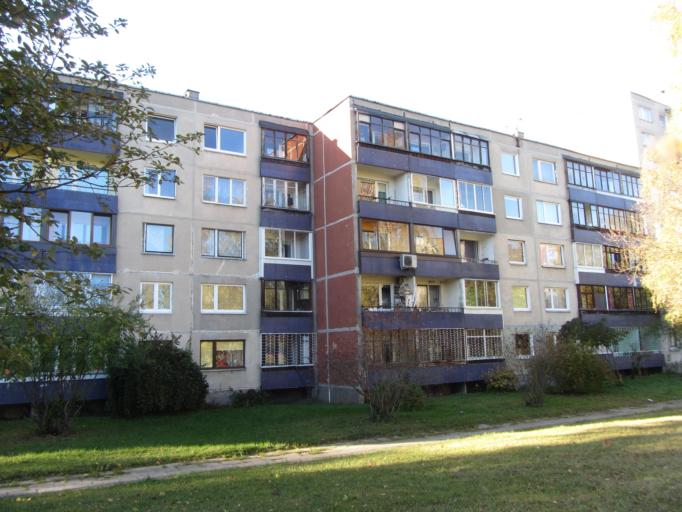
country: LT
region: Vilnius County
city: Justiniskes
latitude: 54.6955
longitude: 25.2236
